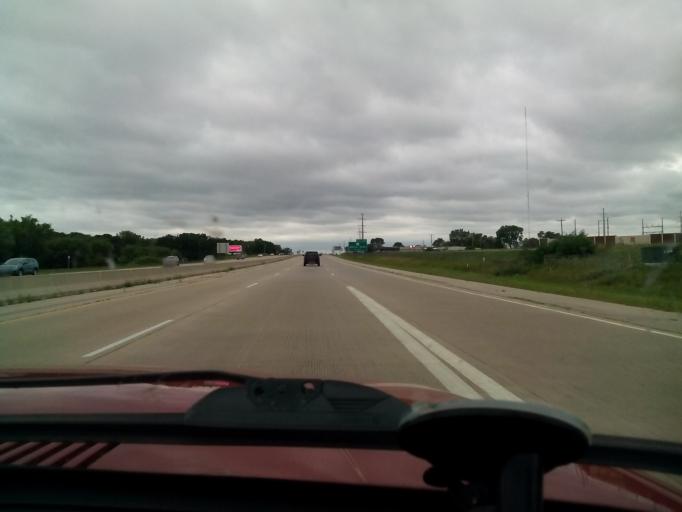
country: US
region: Wisconsin
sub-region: Dane County
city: Sun Prairie
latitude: 43.1717
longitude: -89.2551
